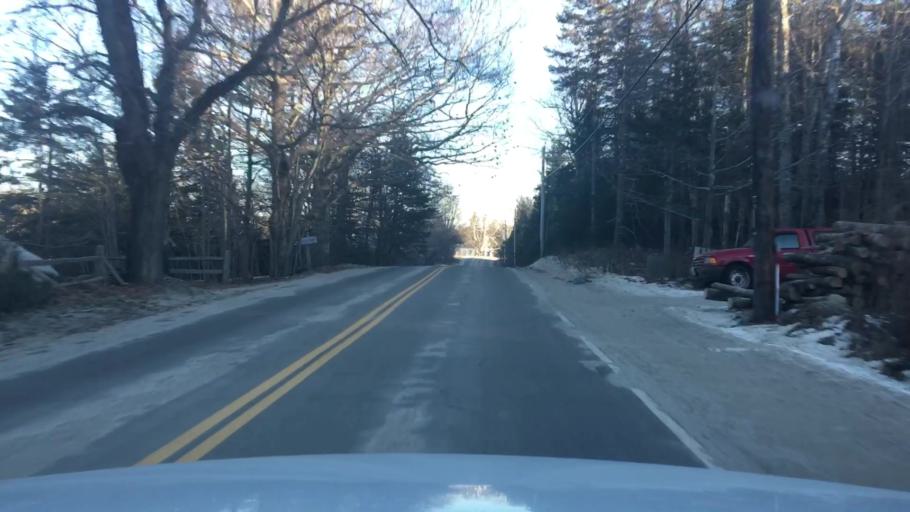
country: US
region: Maine
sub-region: Hancock County
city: Penobscot
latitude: 44.3896
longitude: -68.7023
